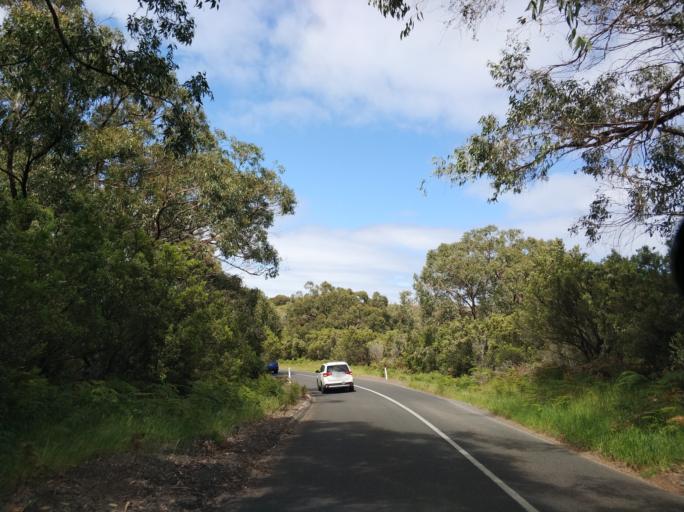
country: AU
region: Victoria
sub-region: Colac-Otway
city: Apollo Bay
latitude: -38.8452
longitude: 143.5329
